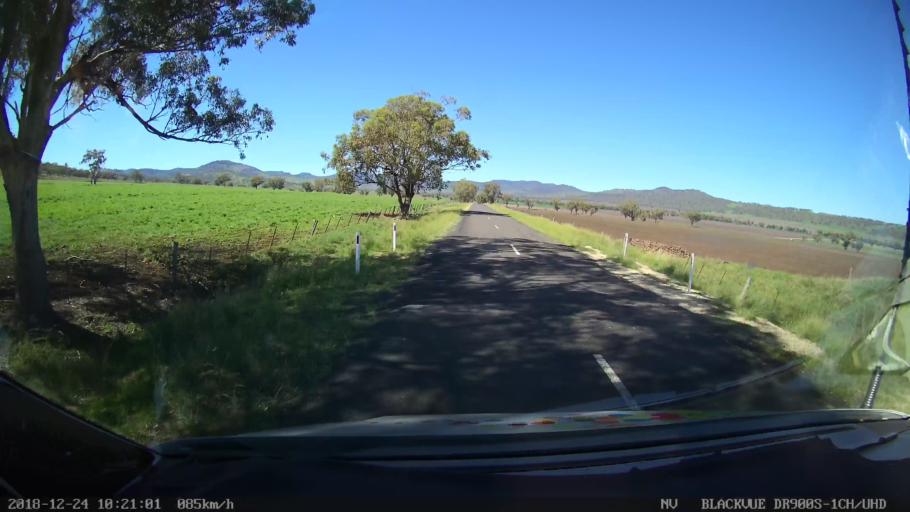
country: AU
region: New South Wales
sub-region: Liverpool Plains
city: Quirindi
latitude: -31.7474
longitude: 150.5535
